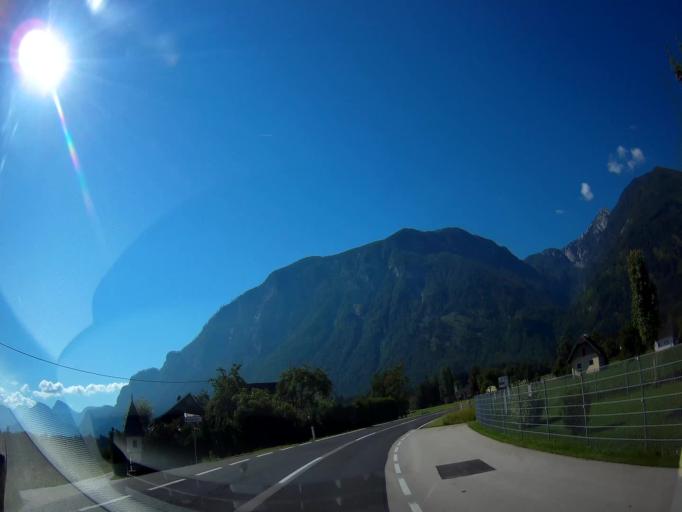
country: AT
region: Carinthia
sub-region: Politischer Bezirk Volkermarkt
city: Gallizien
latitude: 46.5511
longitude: 14.5136
